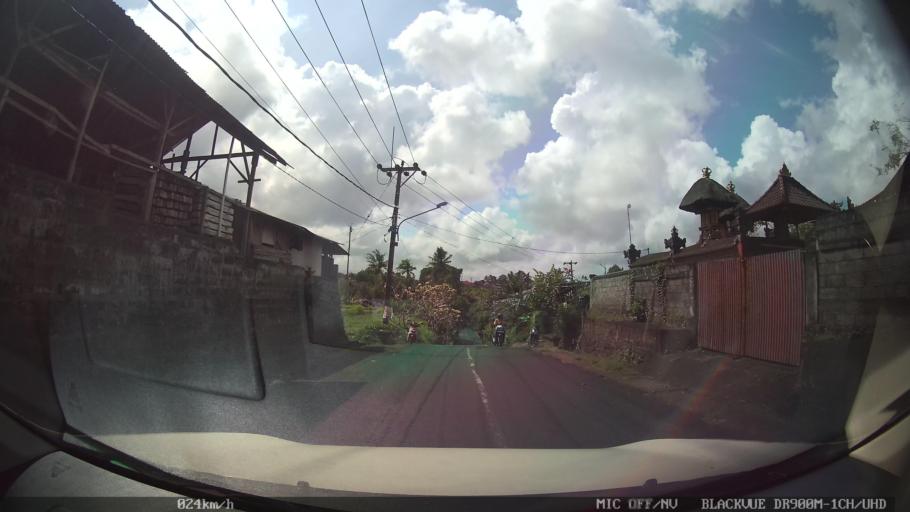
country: ID
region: Bali
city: Banjar Karangsuling
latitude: -8.5992
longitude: 115.1970
